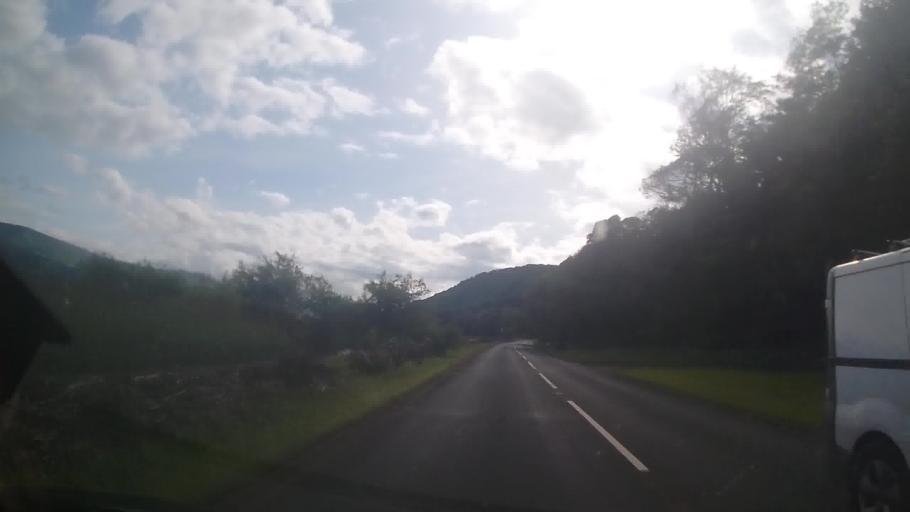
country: GB
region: Wales
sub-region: Gwynedd
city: Barmouth
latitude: 52.7350
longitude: -4.0241
